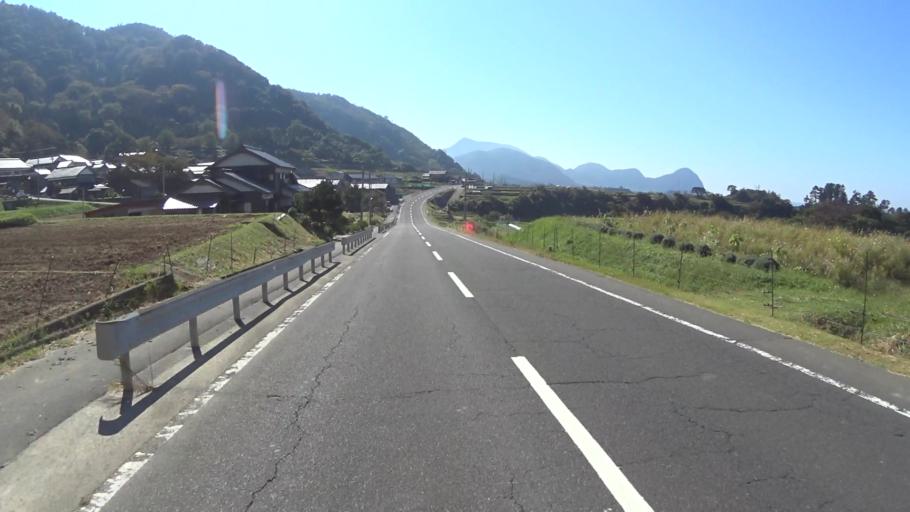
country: JP
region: Kyoto
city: Miyazu
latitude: 35.7646
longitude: 135.1925
